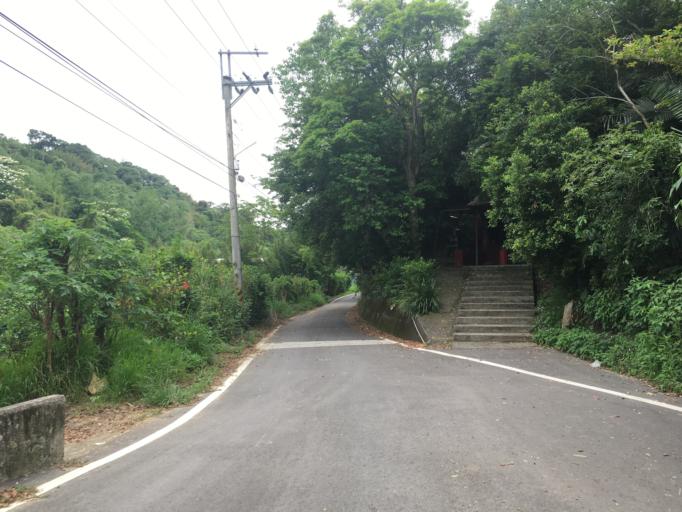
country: TW
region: Taiwan
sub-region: Hsinchu
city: Hsinchu
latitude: 24.7381
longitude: 120.9801
